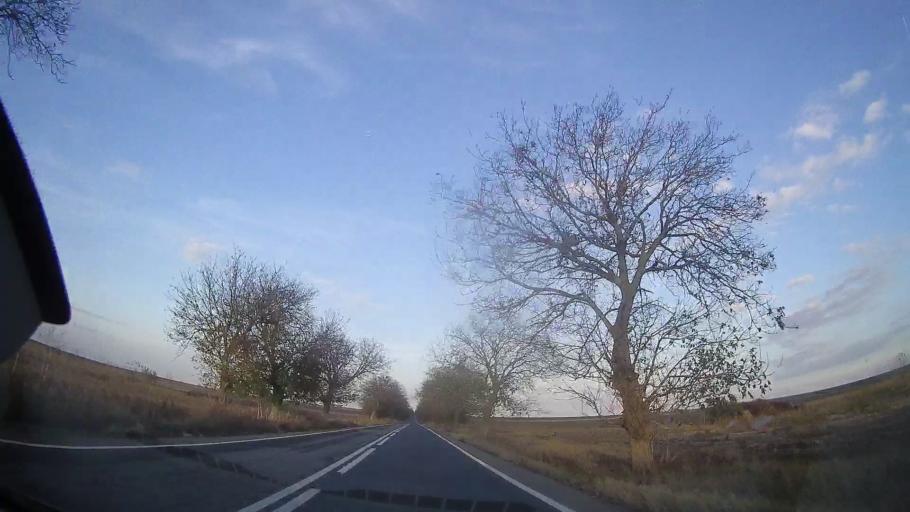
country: RO
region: Constanta
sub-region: Comuna Chirnogeni
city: Chirnogeni
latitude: 43.8553
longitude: 28.2493
